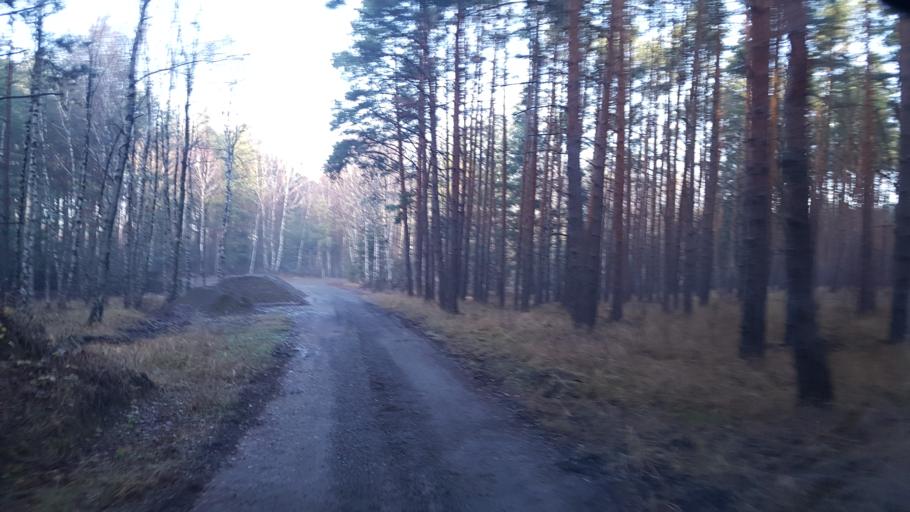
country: DE
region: Brandenburg
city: Trobitz
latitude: 51.5792
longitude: 13.4585
